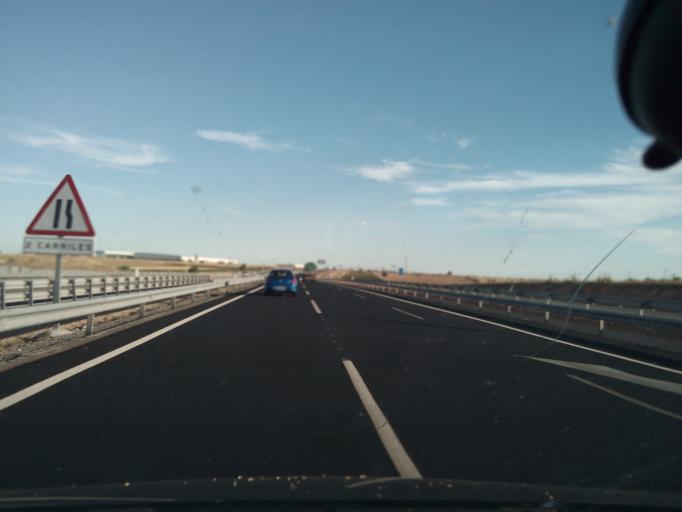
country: ES
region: Castille-La Mancha
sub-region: Province of Toledo
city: Dosbarrios
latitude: 39.9038
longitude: -3.4741
